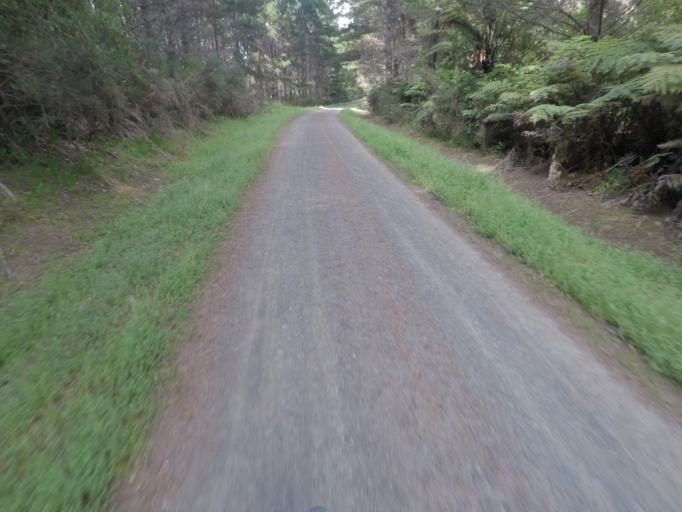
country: NZ
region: Auckland
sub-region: Auckland
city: Muriwai Beach
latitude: -36.7455
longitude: 174.5651
